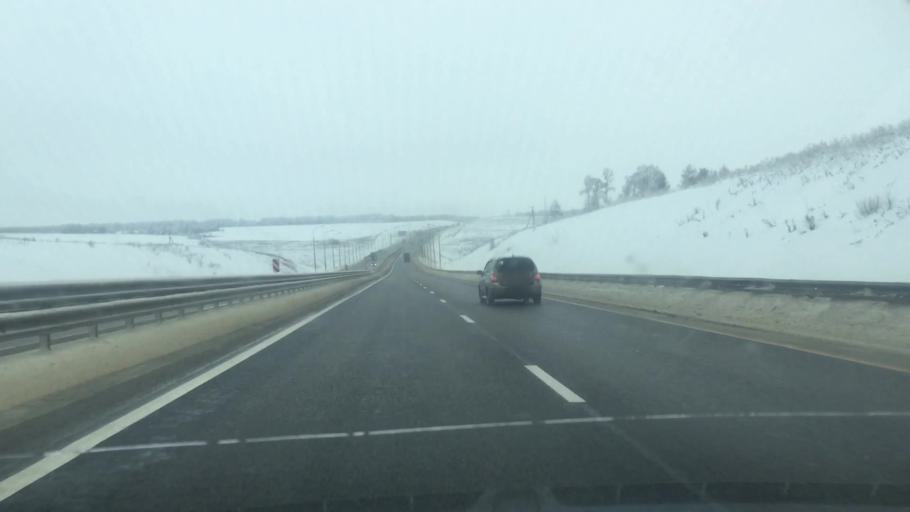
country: RU
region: Lipetsk
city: Stanovoye
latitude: 52.8691
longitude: 38.2823
